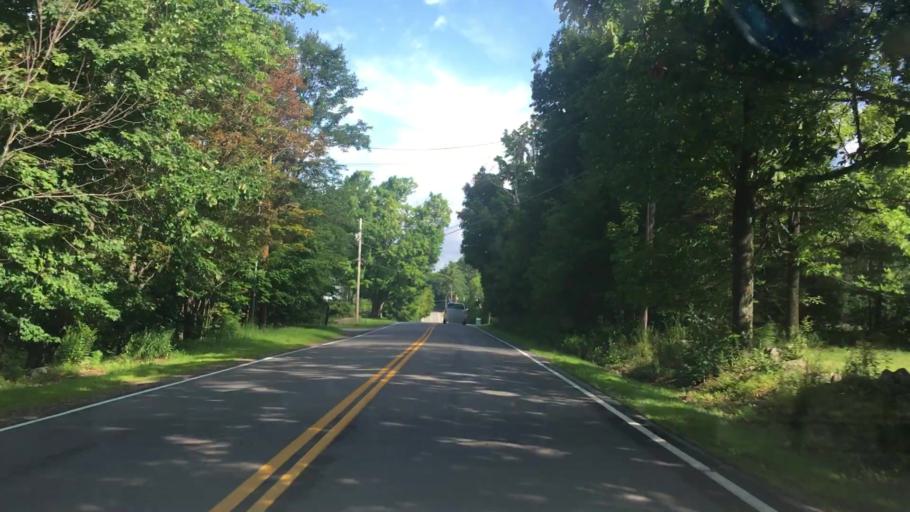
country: US
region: New Hampshire
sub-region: Belknap County
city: Gilford
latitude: 43.5380
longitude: -71.3477
